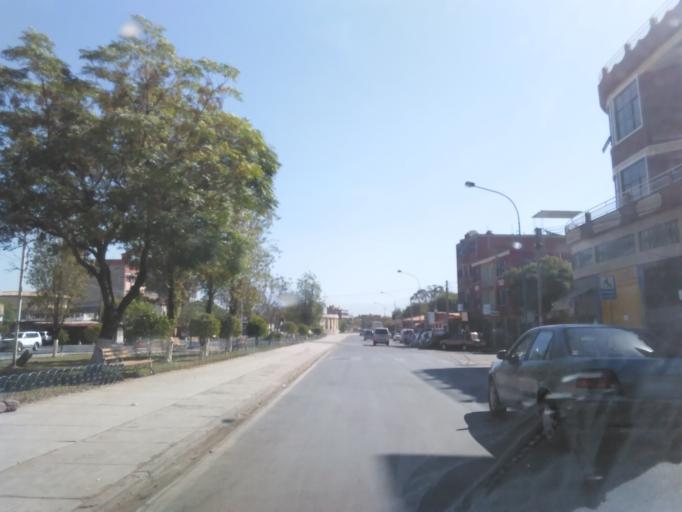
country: BO
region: Cochabamba
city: Cochabamba
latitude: -17.4133
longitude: -66.1569
